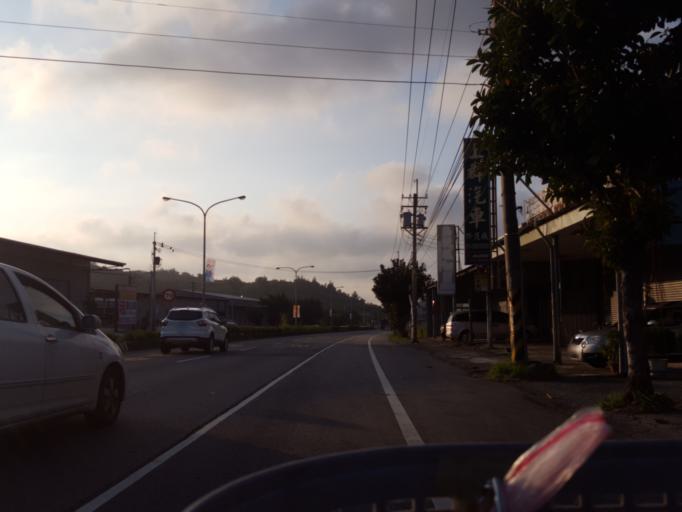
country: TW
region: Taiwan
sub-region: Hsinchu
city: Zhubei
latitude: 24.8821
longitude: 121.0313
